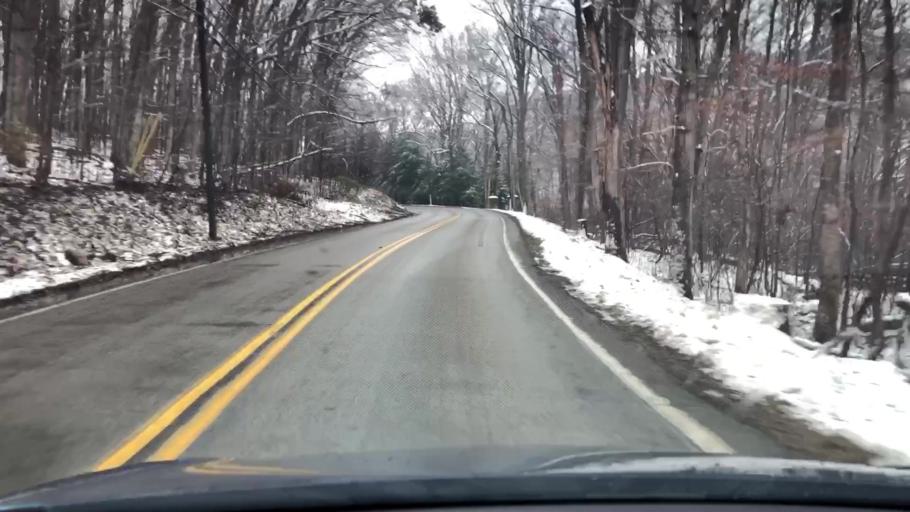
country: US
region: Pennsylvania
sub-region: Fayette County
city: Hopwood
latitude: 39.8189
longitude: -79.5497
